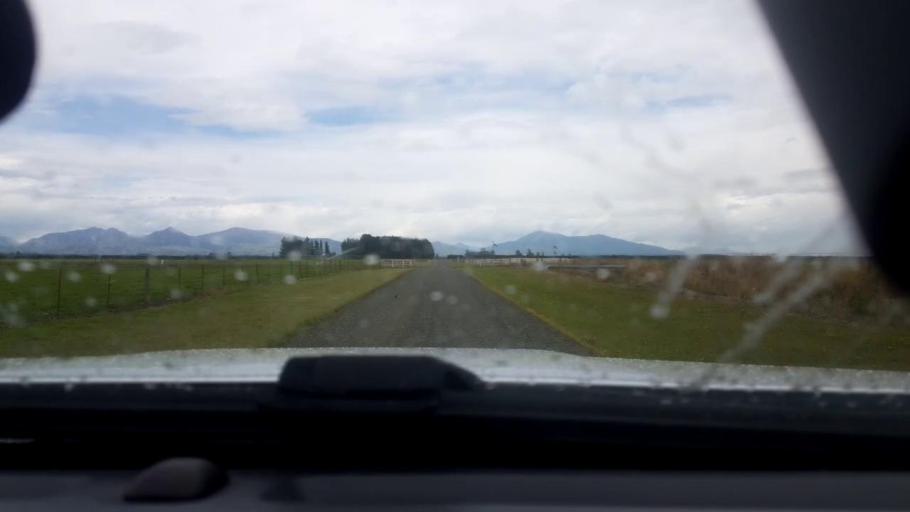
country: NZ
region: Canterbury
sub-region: Timaru District
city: Pleasant Point
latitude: -44.1144
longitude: 171.3550
